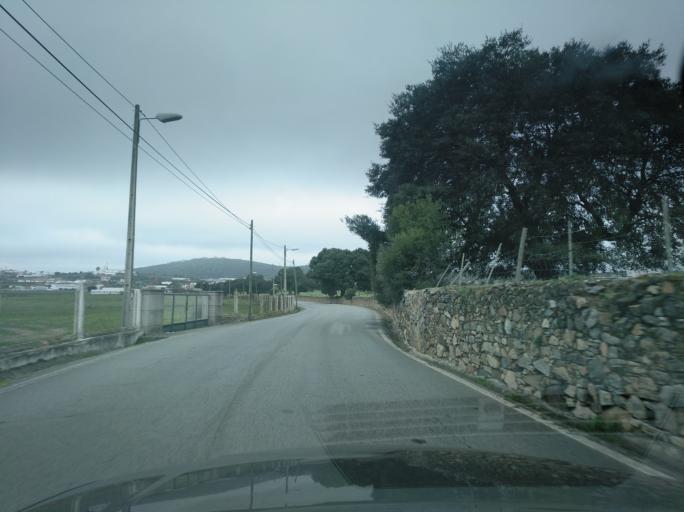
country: PT
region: Portalegre
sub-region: Elvas
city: Elvas
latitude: 38.8888
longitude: -7.1324
